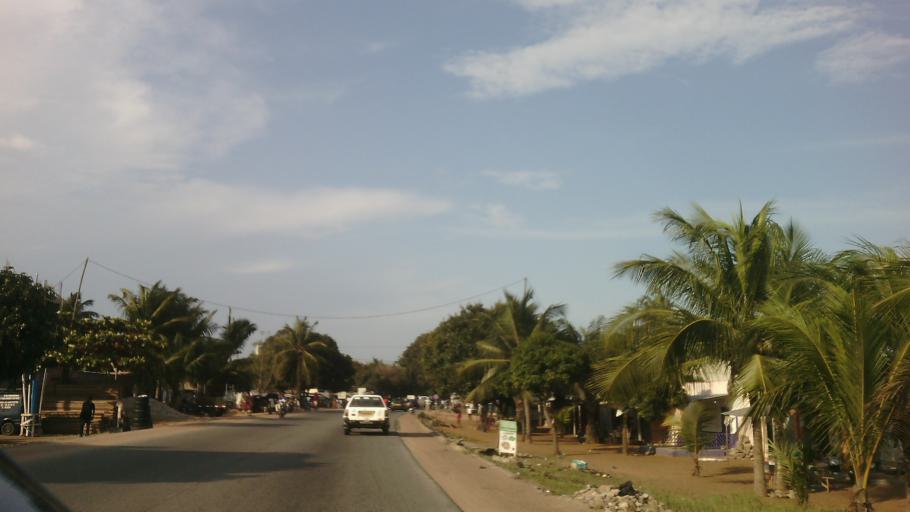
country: TG
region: Maritime
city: Lome
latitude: 6.1910
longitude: 1.3951
